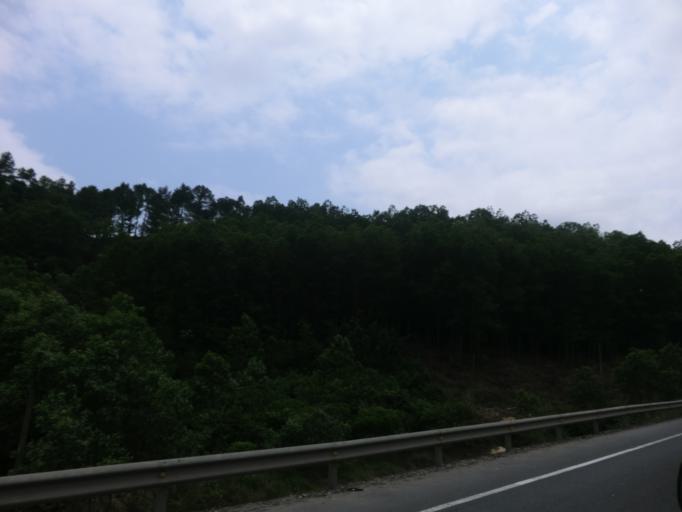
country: VN
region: Thua Thien-Hue
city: Phu Loc
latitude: 16.2756
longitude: 107.9192
